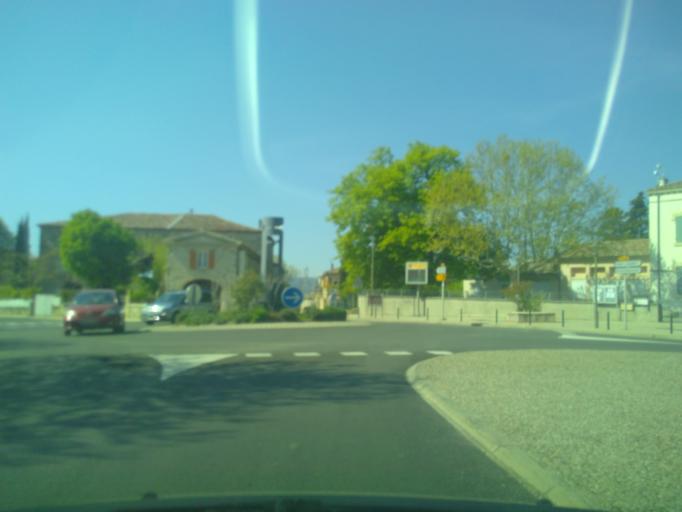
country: FR
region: Rhone-Alpes
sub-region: Departement de la Drome
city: La Begude-de-Mazenc
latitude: 44.5919
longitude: 4.9531
